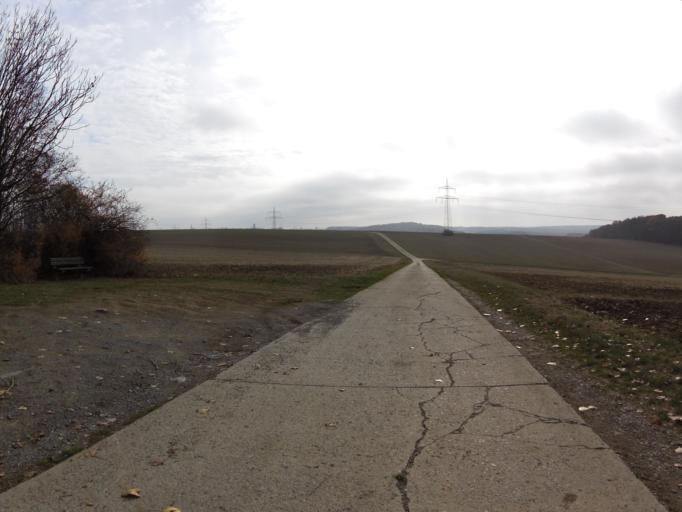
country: DE
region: Bavaria
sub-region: Regierungsbezirk Unterfranken
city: Eisingen
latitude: 49.7583
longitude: 9.8180
